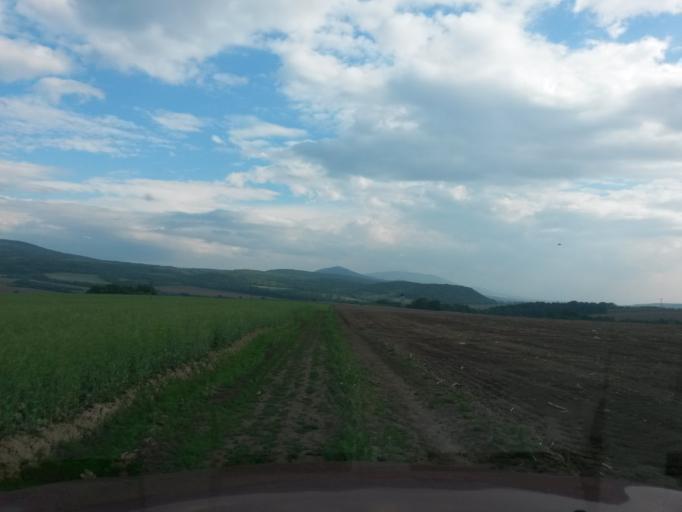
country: SK
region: Kosicky
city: Secovce
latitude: 48.7456
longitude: 21.4613
